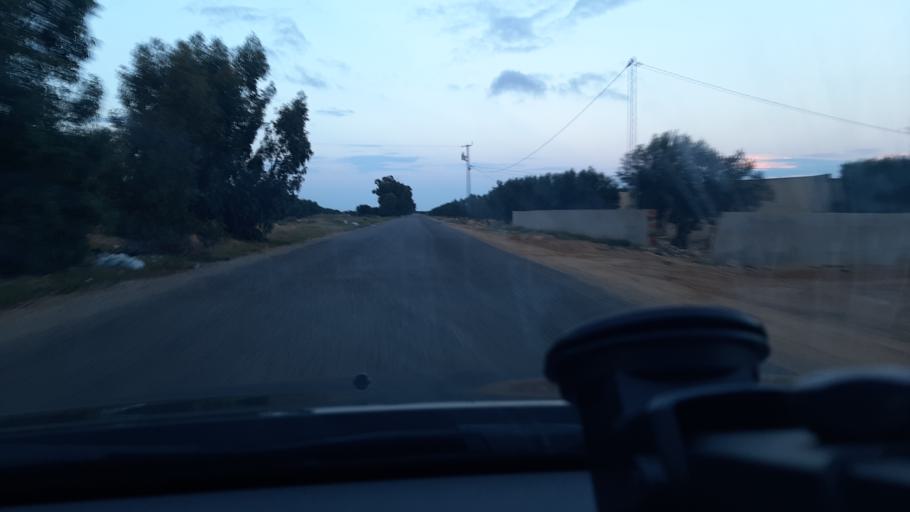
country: TN
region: Al Mahdiyah
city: Shurban
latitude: 34.9747
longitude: 10.3770
